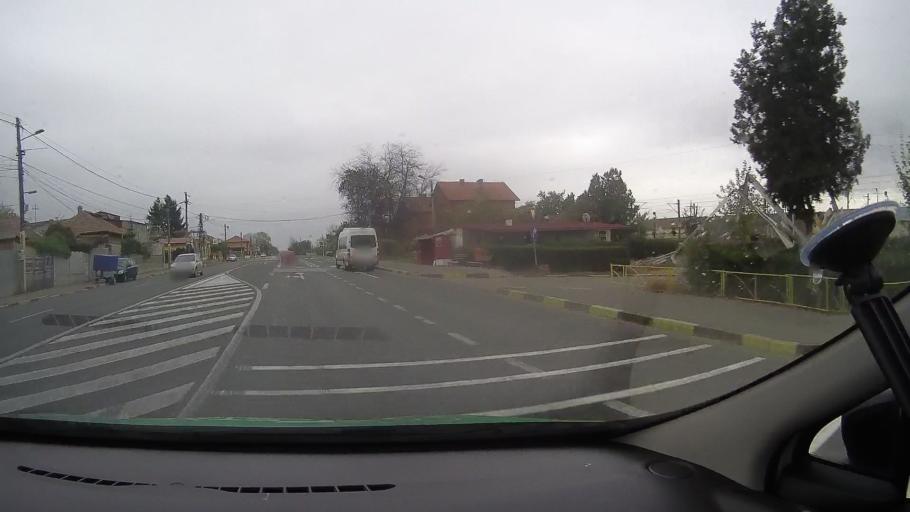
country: RO
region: Constanta
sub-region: Oras Murfatlar
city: Murfatlar
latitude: 44.1723
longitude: 28.4165
